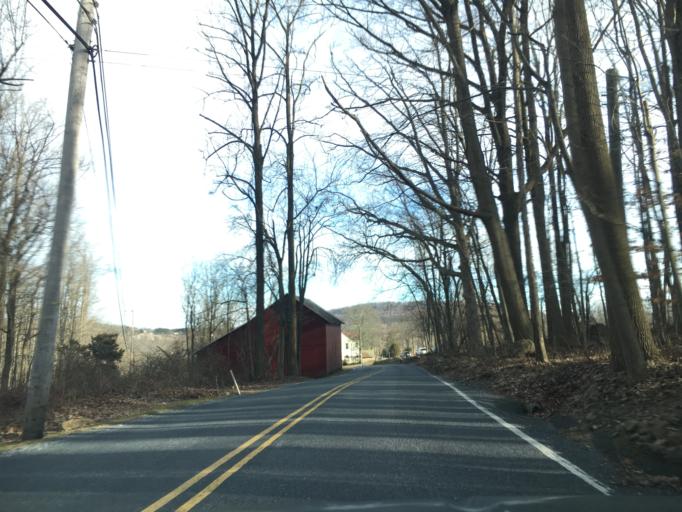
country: US
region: Pennsylvania
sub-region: Berks County
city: Stony Creek Mills
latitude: 40.3803
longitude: -75.8629
